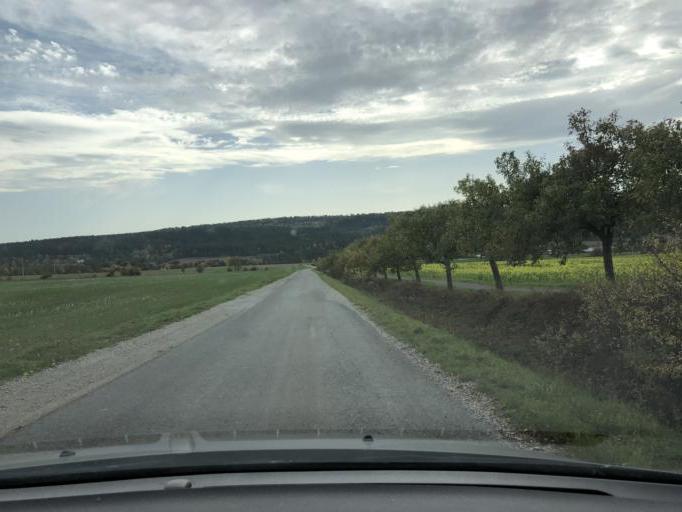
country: DE
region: Thuringia
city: Hohenfelden
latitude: 50.8867
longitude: 11.1642
